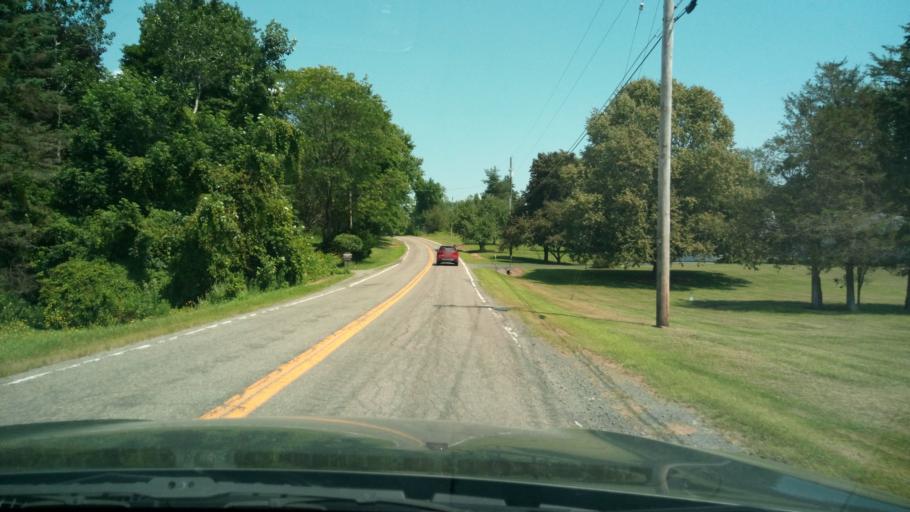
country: US
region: New York
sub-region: Chemung County
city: Horseheads North
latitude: 42.2515
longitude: -76.8011
